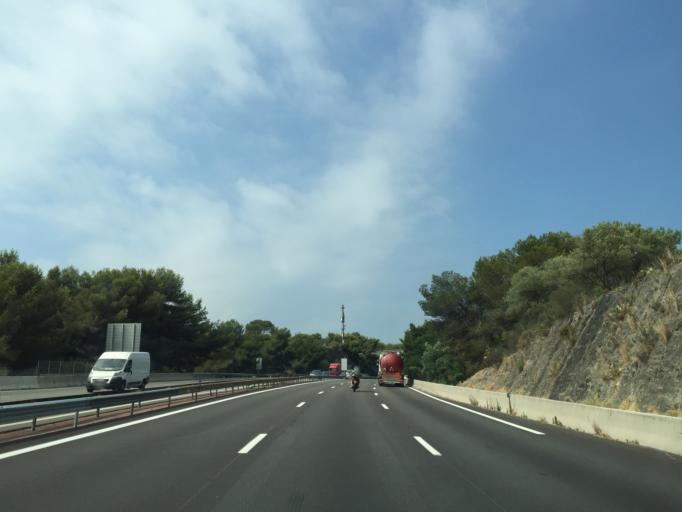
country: FR
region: Provence-Alpes-Cote d'Azur
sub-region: Departement des Alpes-Maritimes
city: Biot
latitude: 43.6344
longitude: 7.1260
